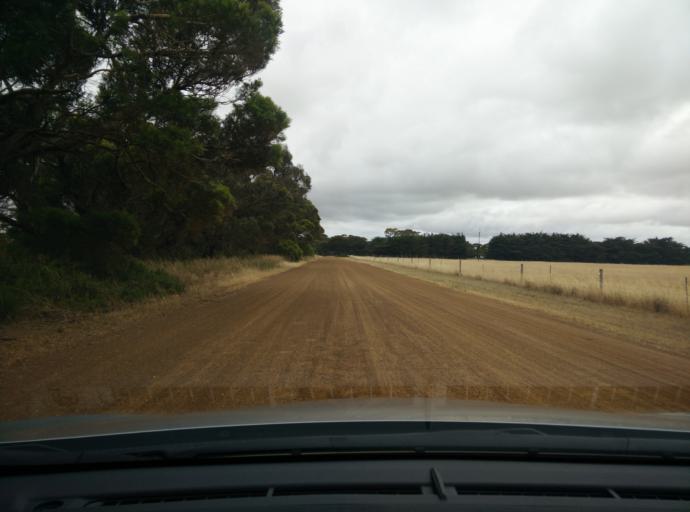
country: AU
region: South Australia
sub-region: Kangaroo Island
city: Kingscote
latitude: -35.8311
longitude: 137.5614
